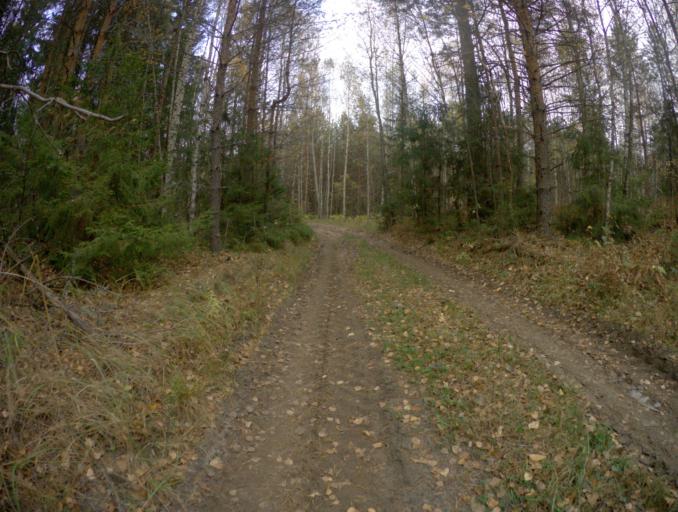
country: RU
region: Vladimir
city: Raduzhnyy
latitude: 55.9306
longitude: 40.3544
